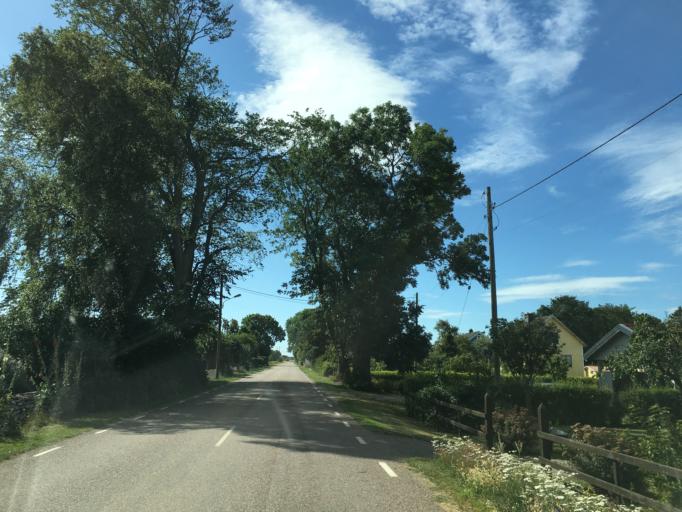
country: SE
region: Kalmar
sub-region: Morbylanga Kommun
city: Moerbylanga
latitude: 56.3908
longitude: 16.4130
